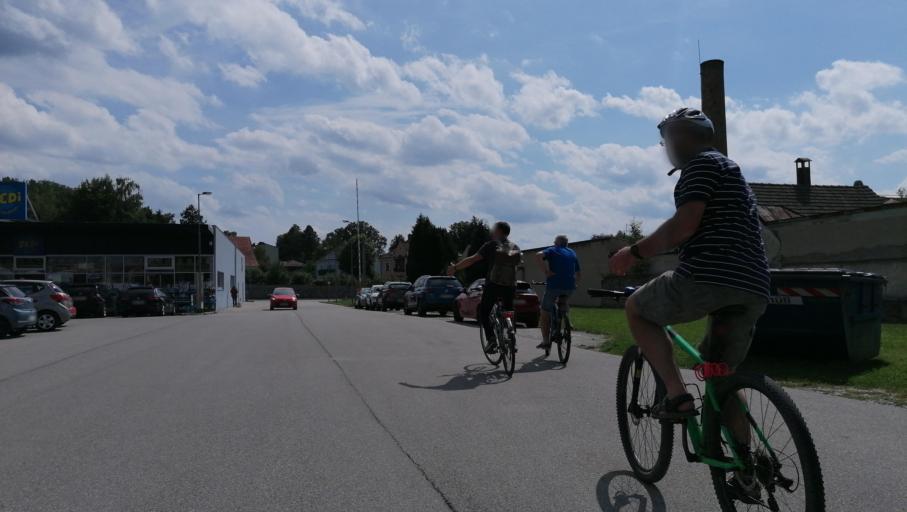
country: AT
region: Lower Austria
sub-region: Politischer Bezirk Gmund
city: Schrems
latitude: 48.7908
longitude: 15.0699
